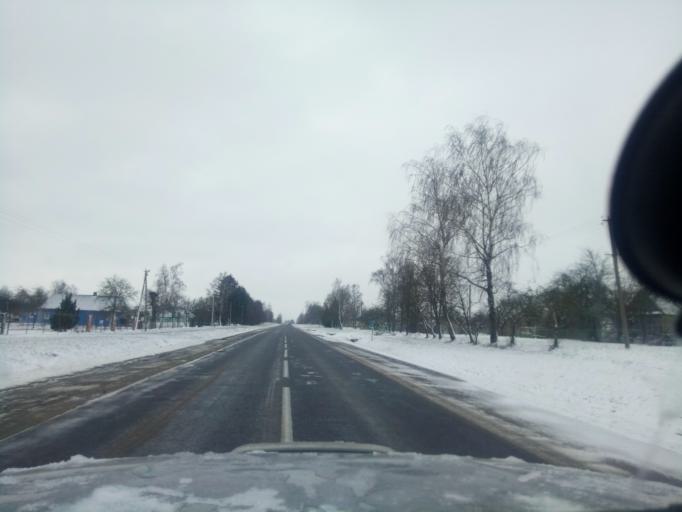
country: BY
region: Minsk
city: Klyetsk
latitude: 53.1227
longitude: 26.6669
